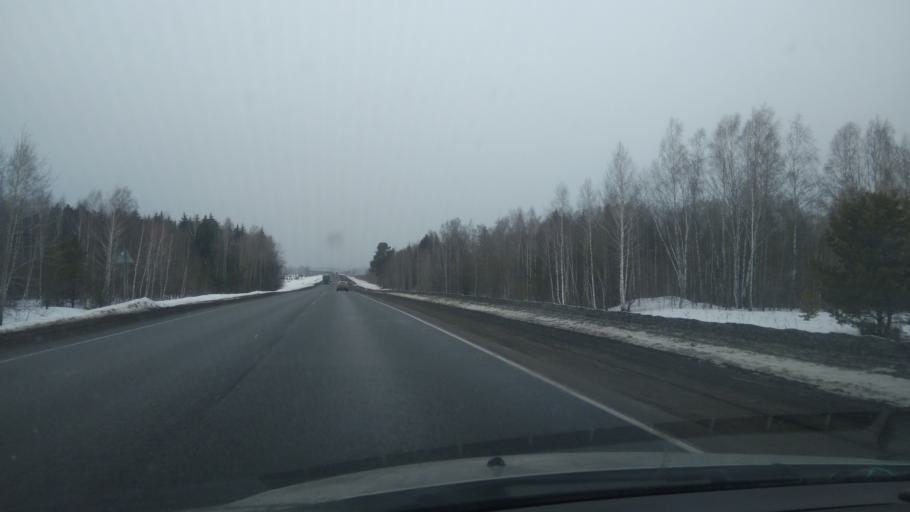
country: RU
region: Perm
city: Orda
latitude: 57.2472
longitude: 57.0456
